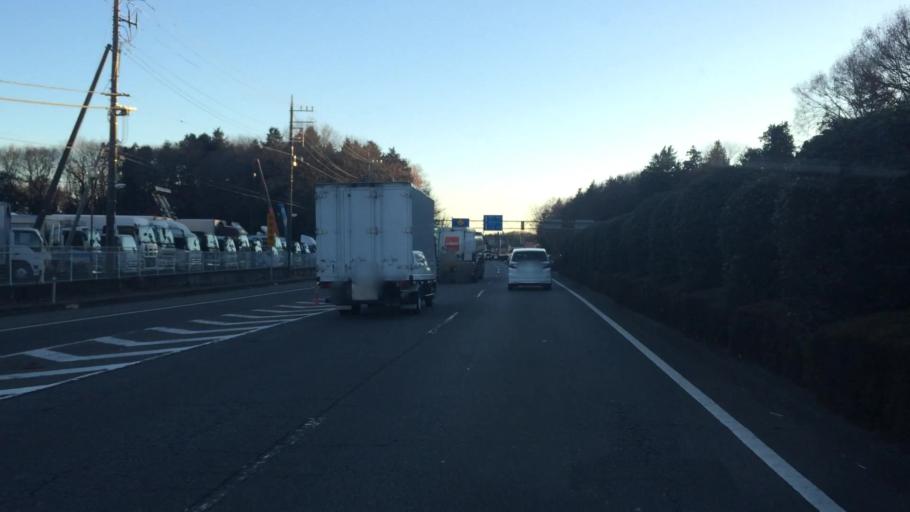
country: JP
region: Tochigi
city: Utsunomiya-shi
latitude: 36.5196
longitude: 139.9193
